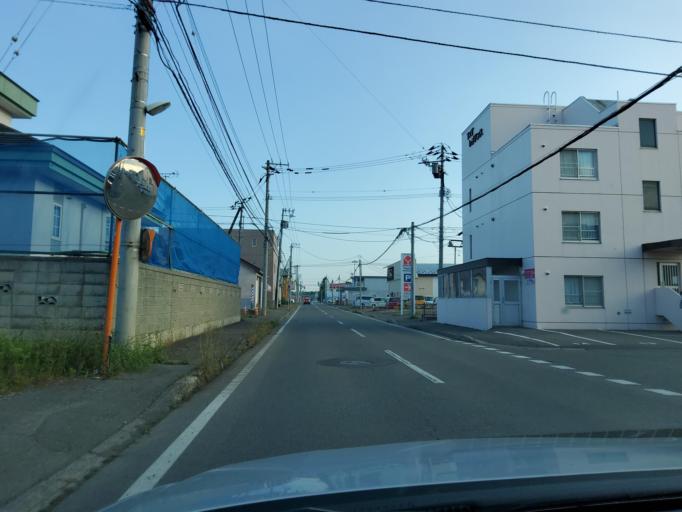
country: JP
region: Hokkaido
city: Obihiro
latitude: 42.9320
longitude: 143.1836
